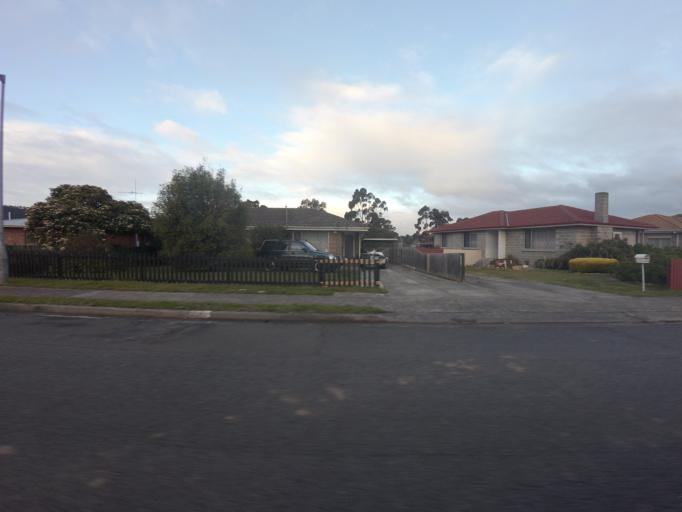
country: AU
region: Tasmania
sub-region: Clarence
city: Rokeby
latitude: -42.9044
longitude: 147.4337
